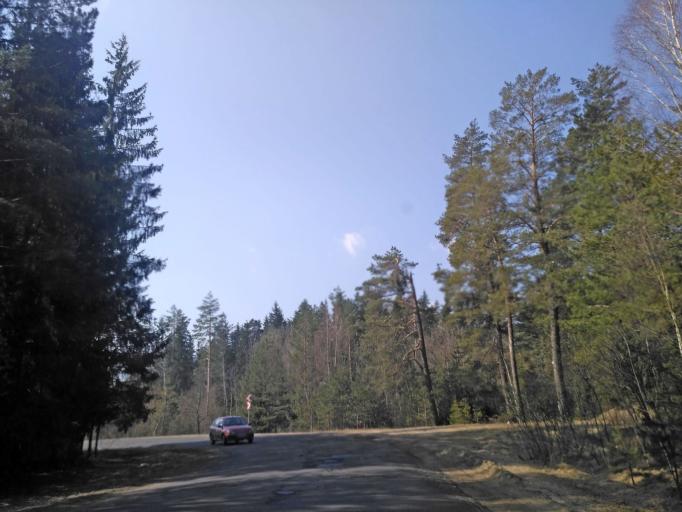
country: BY
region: Minsk
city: Horad Barysaw
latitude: 54.2441
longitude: 28.4502
